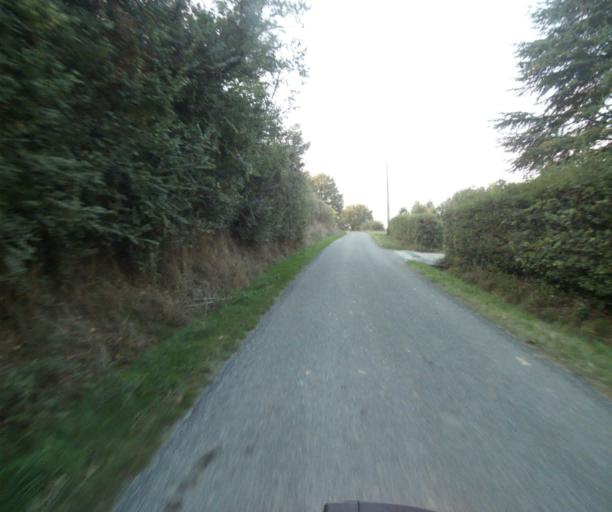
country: FR
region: Midi-Pyrenees
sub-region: Departement du Tarn-et-Garonne
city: Verdun-sur-Garonne
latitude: 43.8247
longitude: 1.2105
